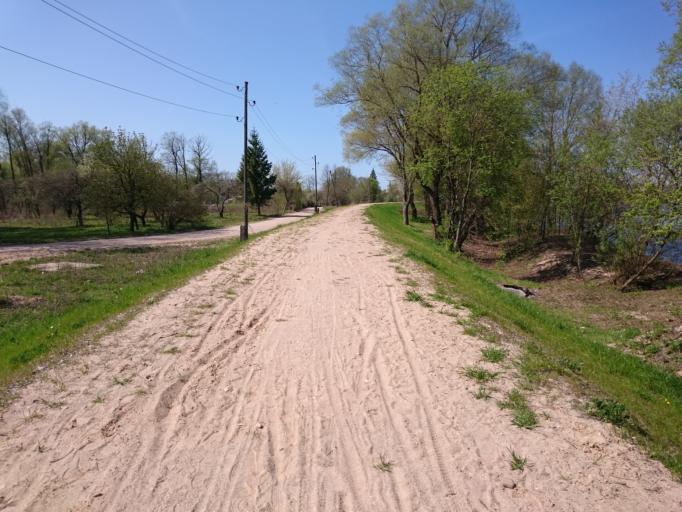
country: LV
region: Adazi
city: Adazi
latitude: 57.0813
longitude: 24.3297
